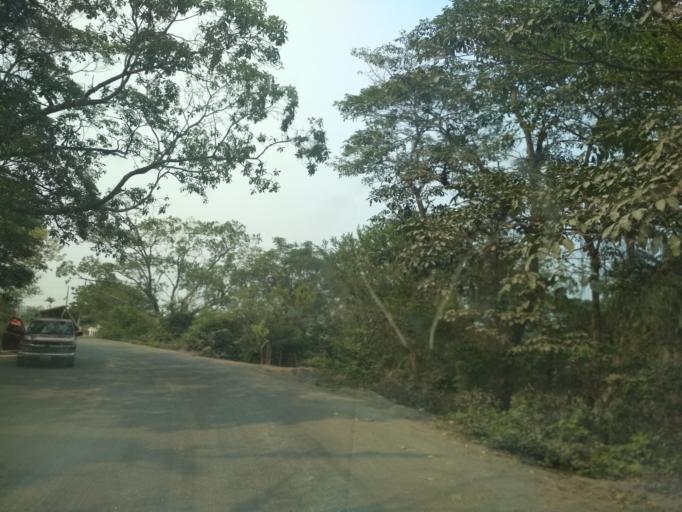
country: MX
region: Veracruz
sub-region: Veracruz
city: Delfino Victoria (Santa Fe)
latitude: 19.1934
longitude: -96.2869
